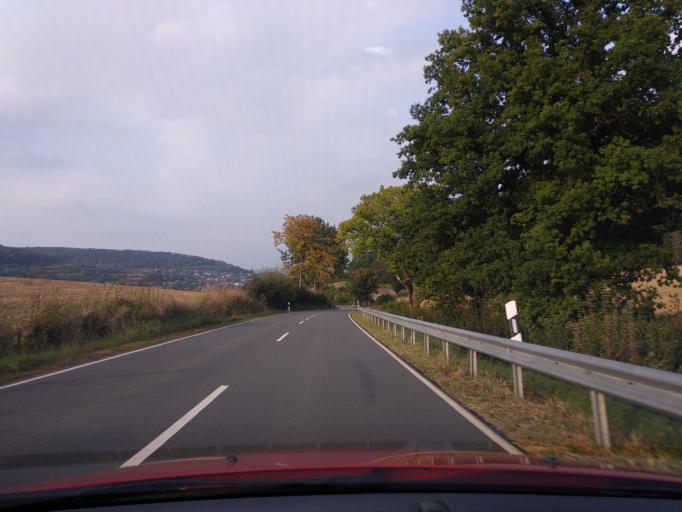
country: DE
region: North Rhine-Westphalia
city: Beverungen
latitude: 51.6497
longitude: 9.3488
